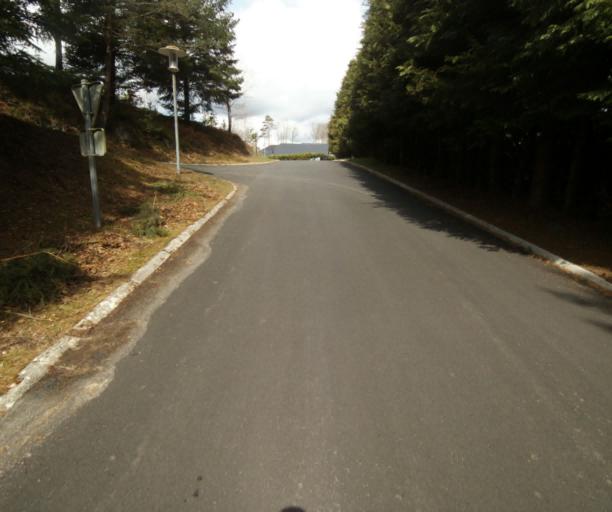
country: FR
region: Limousin
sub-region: Departement de la Correze
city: Correze
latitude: 45.3757
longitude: 1.9417
